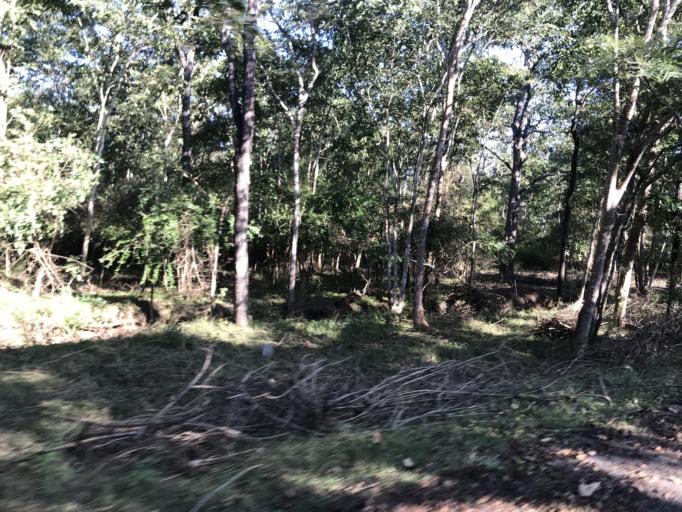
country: IN
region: Karnataka
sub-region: Mysore
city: Heggadadevankote
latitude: 11.9833
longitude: 76.2323
